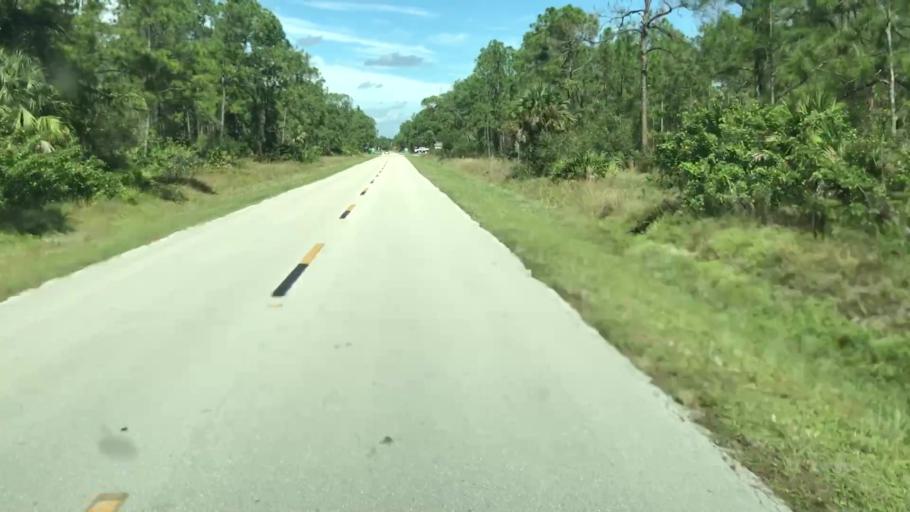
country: US
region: Florida
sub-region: Lee County
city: Lehigh Acres
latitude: 26.6555
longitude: -81.6464
